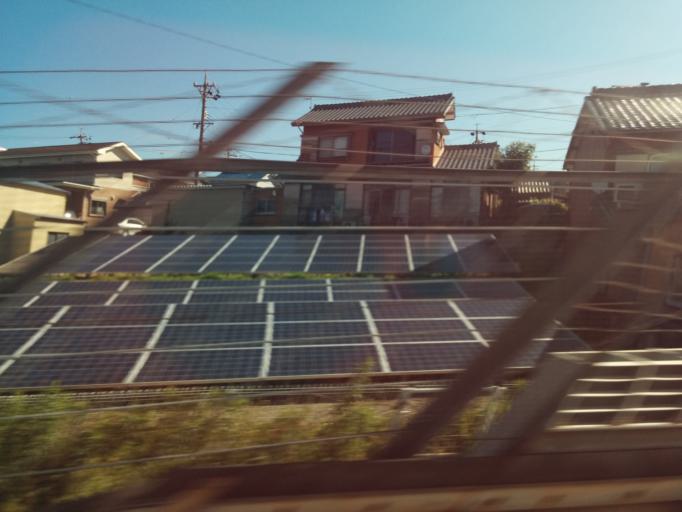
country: JP
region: Aichi
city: Gamagori
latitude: 34.8191
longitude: 137.2534
